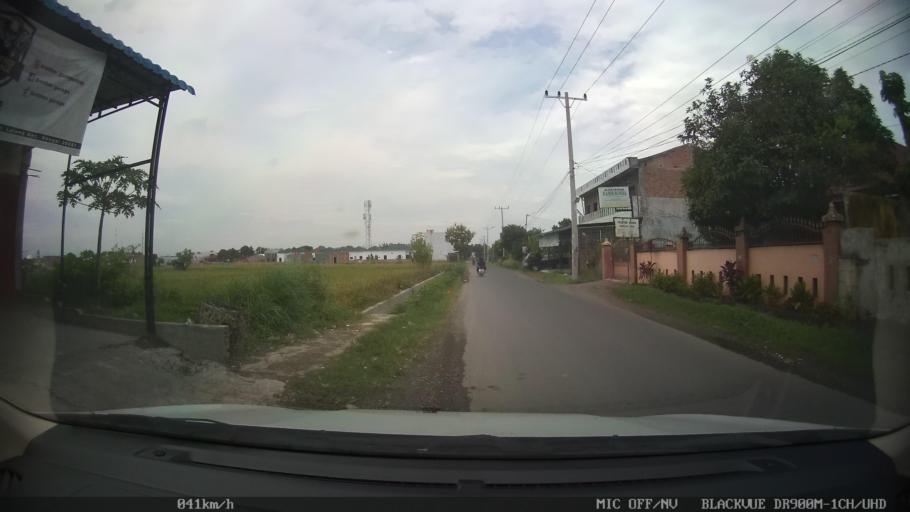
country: ID
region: North Sumatra
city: Sunggal
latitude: 3.6134
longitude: 98.5992
